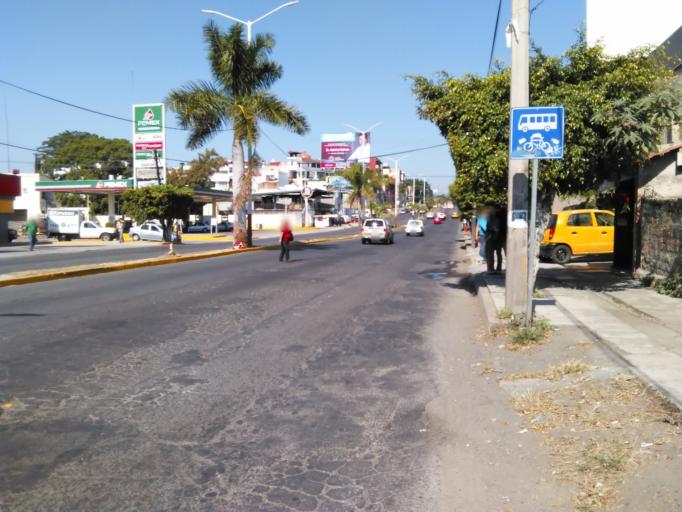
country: MX
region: Nayarit
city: Tepic
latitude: 21.4939
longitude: -104.8962
